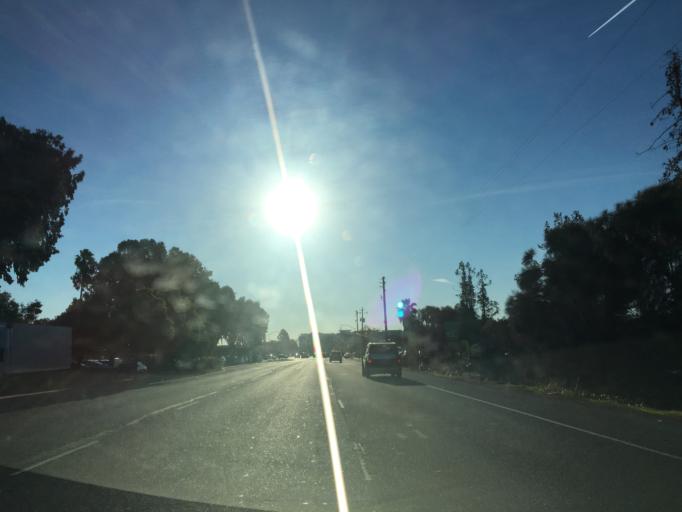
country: US
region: California
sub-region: San Mateo County
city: Redwood City
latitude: 37.4963
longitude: -122.2365
